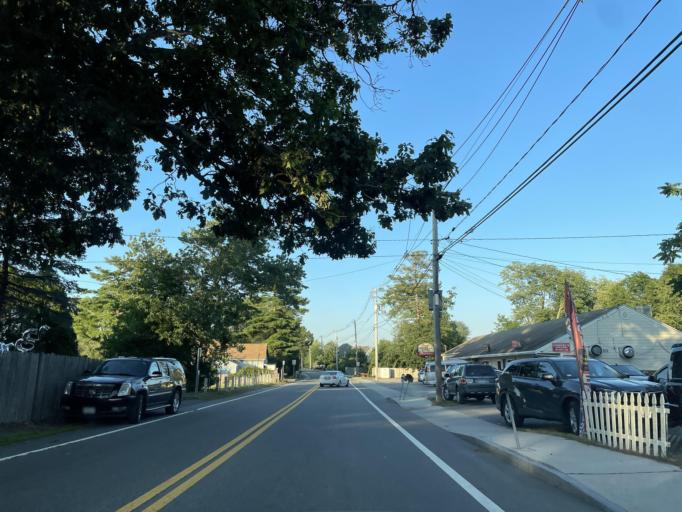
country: US
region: Massachusetts
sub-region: Plymouth County
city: Hanson
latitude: 42.0588
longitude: -70.8342
